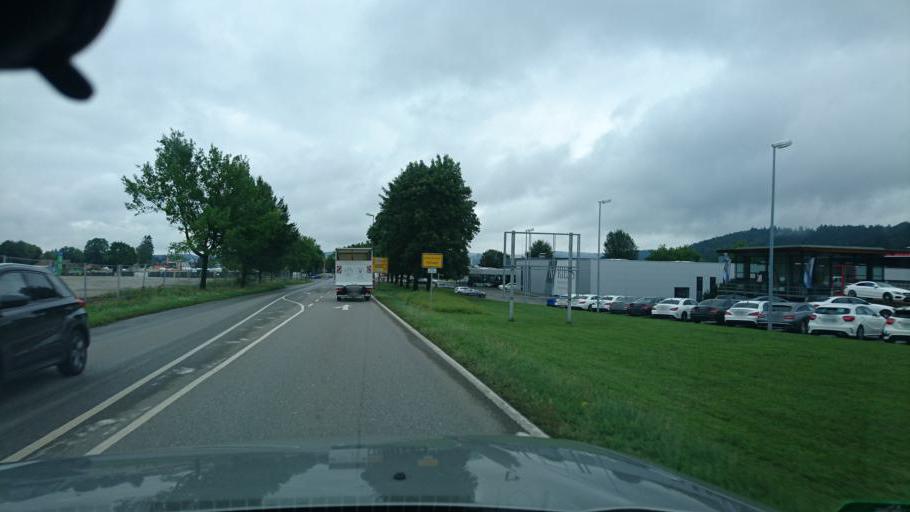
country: DE
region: Baden-Wuerttemberg
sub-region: Freiburg Region
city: Rottweil
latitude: 48.1462
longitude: 8.6399
